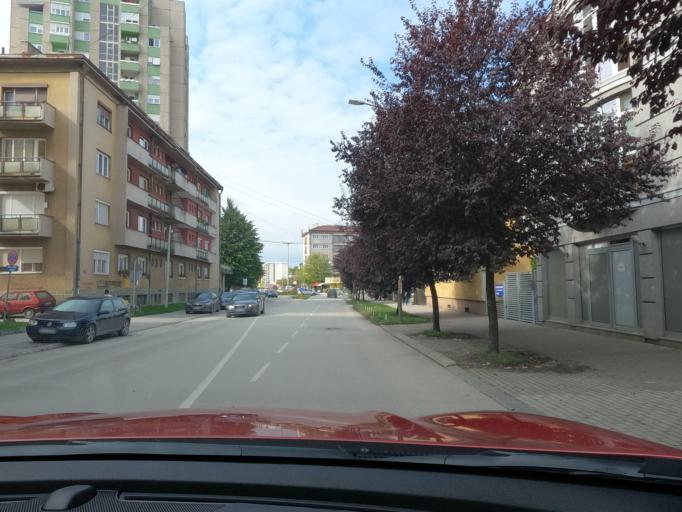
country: RS
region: Central Serbia
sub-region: Moravicki Okrug
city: Cacak
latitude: 43.8872
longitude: 20.3443
